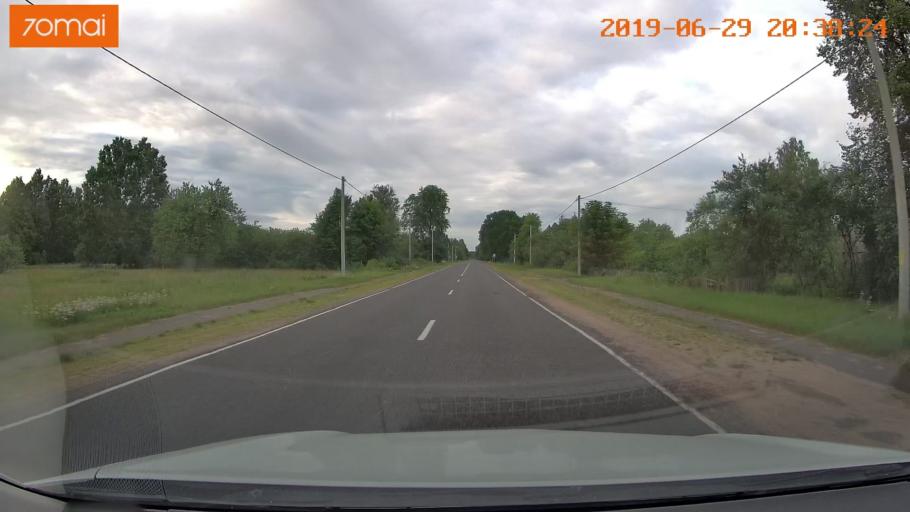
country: BY
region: Brest
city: Hantsavichy
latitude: 52.5496
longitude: 26.3647
